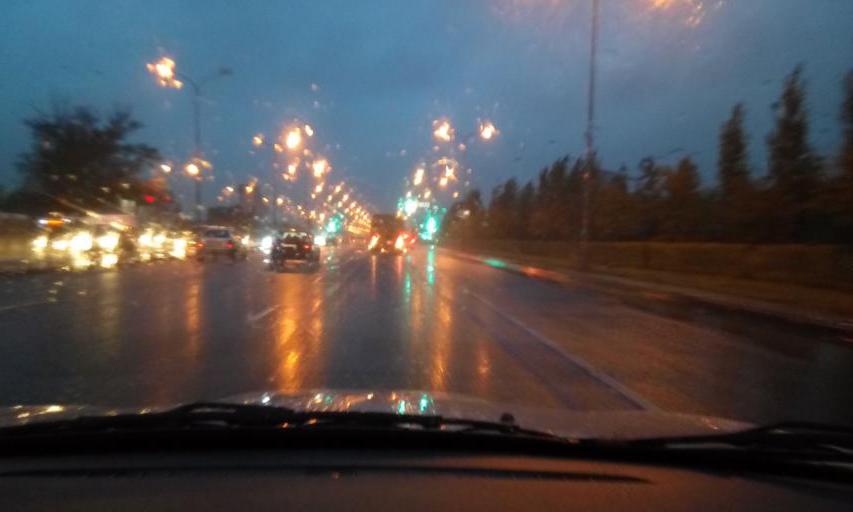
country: KZ
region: Astana Qalasy
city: Astana
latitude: 51.1830
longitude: 71.3673
